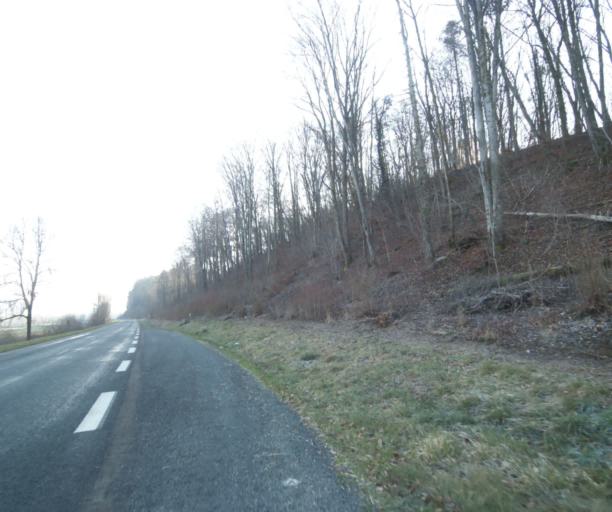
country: FR
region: Champagne-Ardenne
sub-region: Departement de la Haute-Marne
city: Chevillon
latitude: 48.4971
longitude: 5.1206
